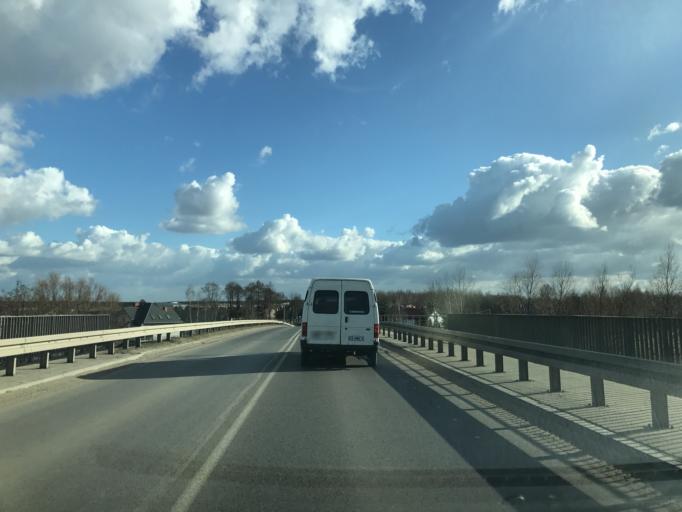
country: PL
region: Masovian Voivodeship
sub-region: Powiat wolominski
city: Radzymin
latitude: 52.4027
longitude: 21.1942
